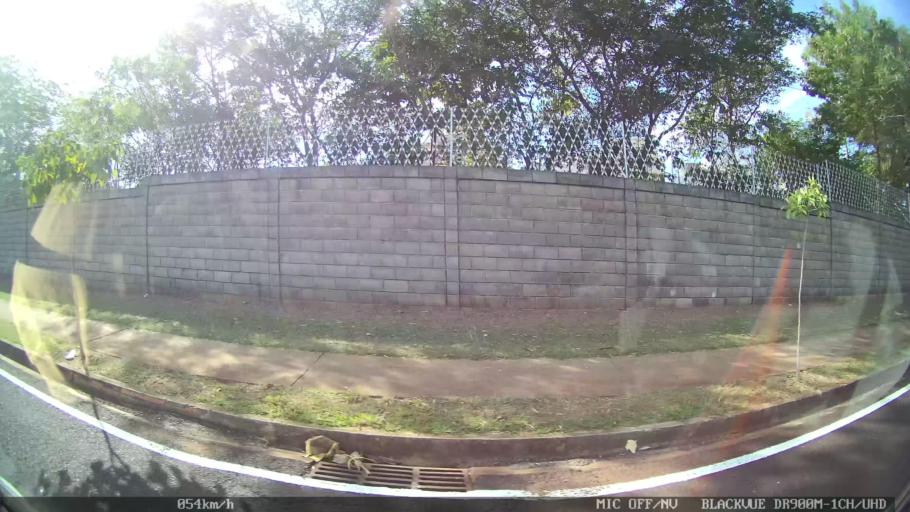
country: BR
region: Sao Paulo
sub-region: Sao Jose Do Rio Preto
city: Sao Jose do Rio Preto
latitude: -20.8106
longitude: -49.3372
